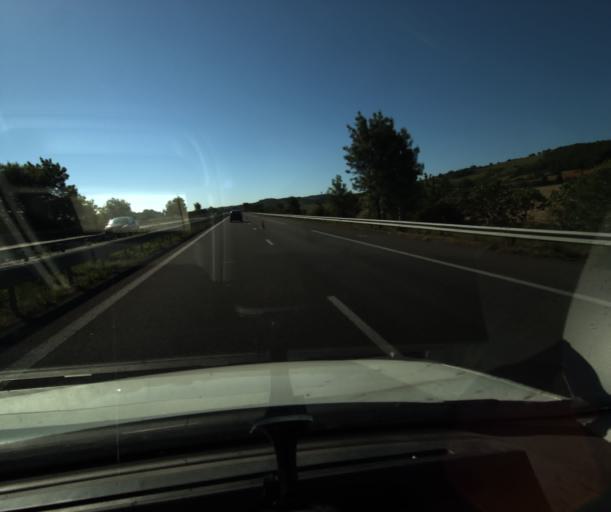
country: FR
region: Midi-Pyrenees
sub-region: Departement de la Haute-Garonne
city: Avignonet-Lauragais
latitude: 43.3314
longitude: 1.8453
